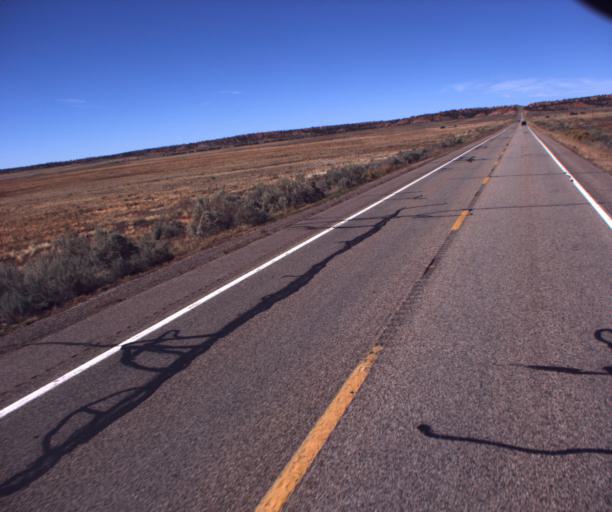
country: US
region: Arizona
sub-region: Mohave County
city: Colorado City
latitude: 36.8737
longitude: -112.8669
